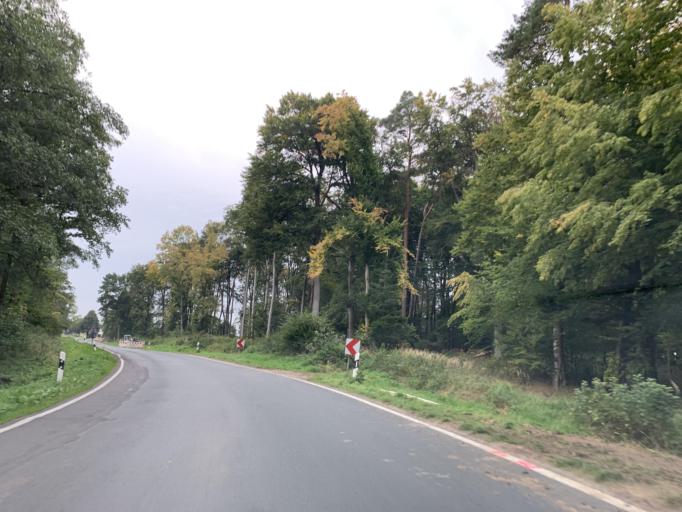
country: DE
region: Mecklenburg-Vorpommern
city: Woldegk
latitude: 53.3354
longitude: 13.6560
